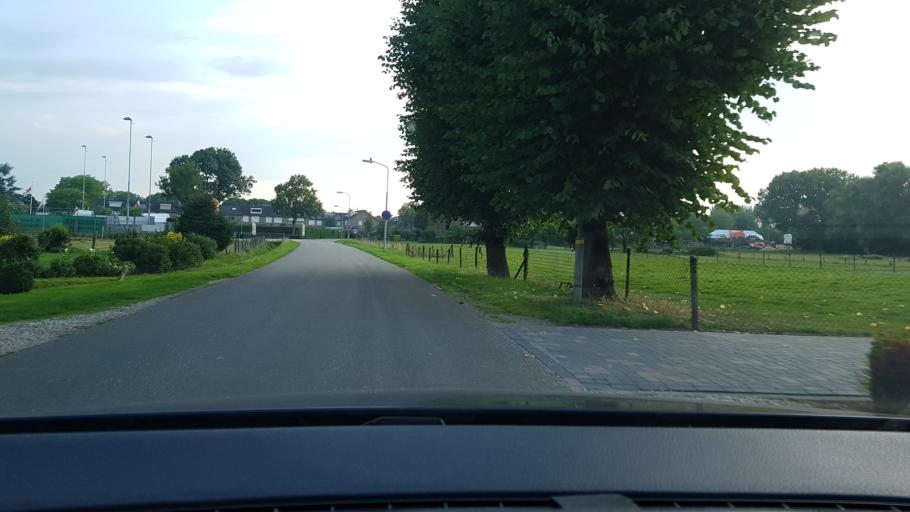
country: NL
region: Gelderland
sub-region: Gemeente Beuningen
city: Beuningen
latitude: 51.8562
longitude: 5.7782
